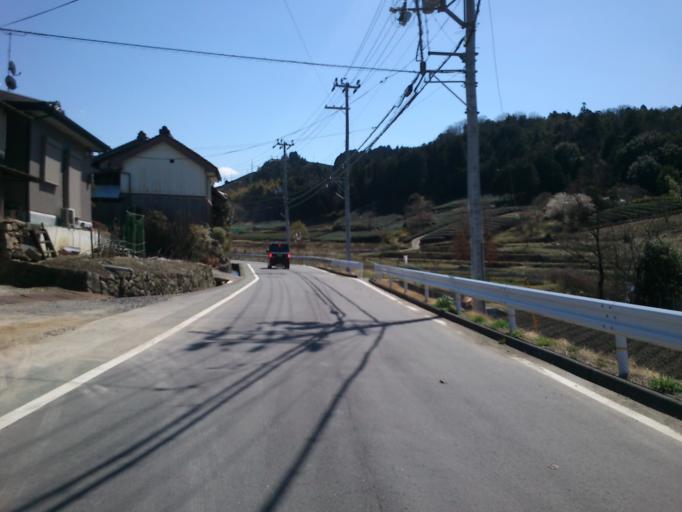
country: JP
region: Kyoto
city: Tanabe
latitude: 34.7879
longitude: 135.9059
